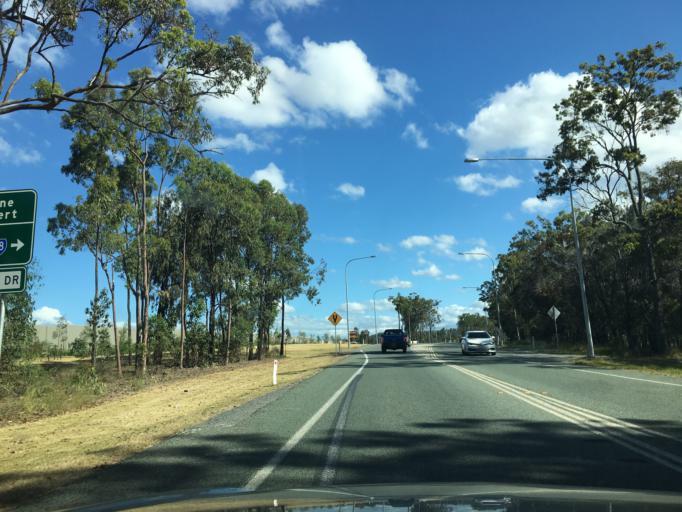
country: AU
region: Queensland
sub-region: Logan
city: Chambers Flat
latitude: -27.7976
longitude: 153.1004
